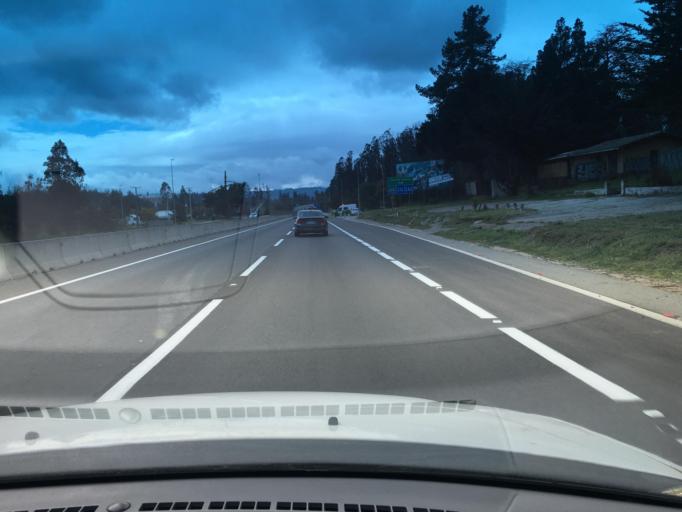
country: CL
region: Valparaiso
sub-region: Provincia de Valparaiso
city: Vina del Mar
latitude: -33.1487
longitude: -71.5588
